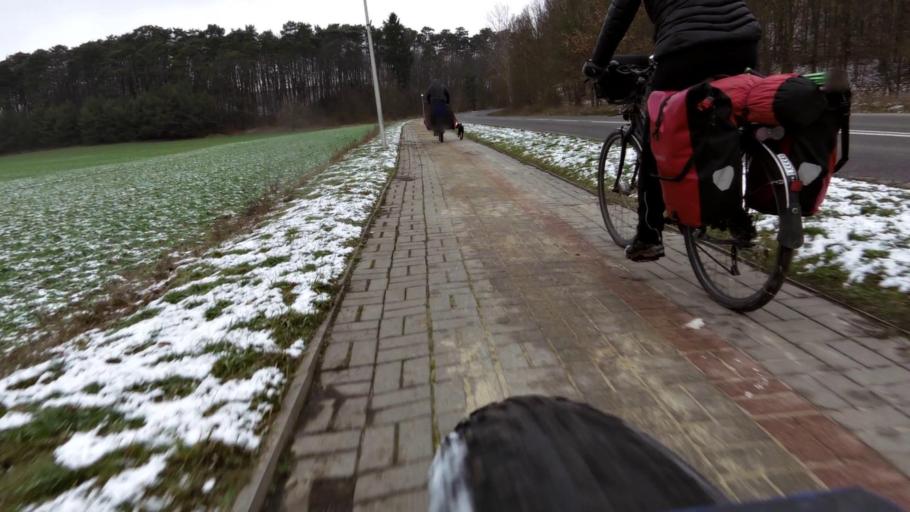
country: PL
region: West Pomeranian Voivodeship
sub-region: Powiat walecki
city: Miroslawiec
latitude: 53.3554
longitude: 16.0854
